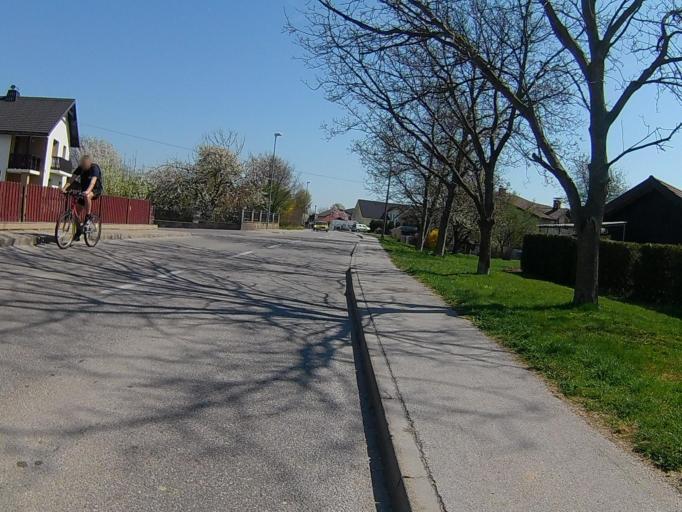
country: SI
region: Hoce-Slivnica
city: Rogoza
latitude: 46.5006
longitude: 15.6728
